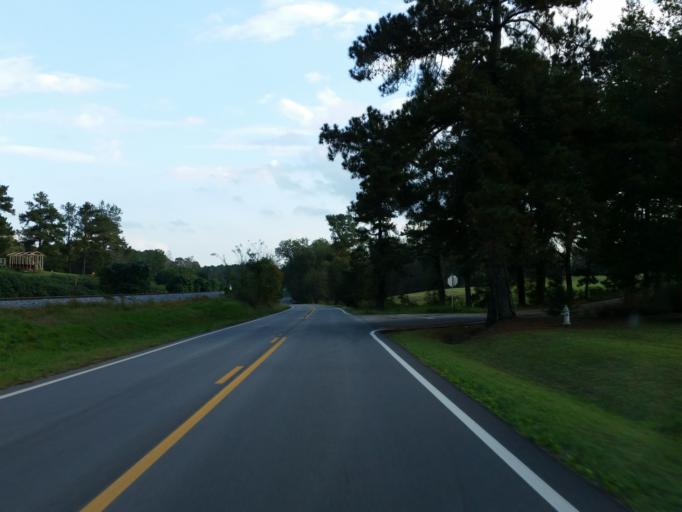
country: US
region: Georgia
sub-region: Monroe County
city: Forsyth
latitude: 32.9748
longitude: -83.8717
